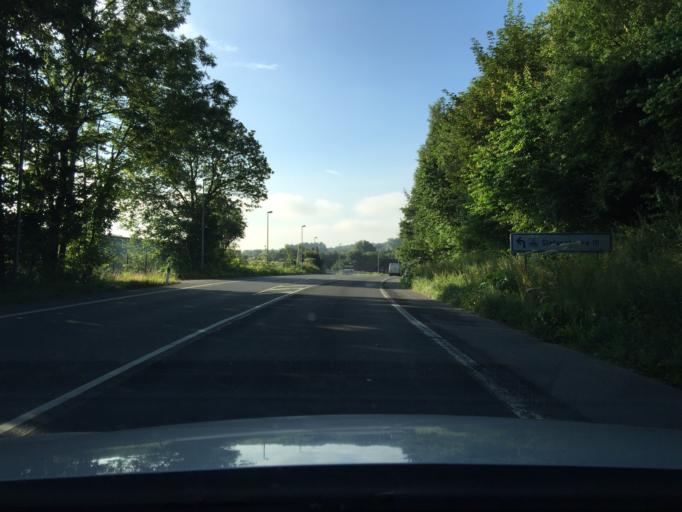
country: DE
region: North Rhine-Westphalia
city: Sprockhovel
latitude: 51.3228
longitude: 7.2711
